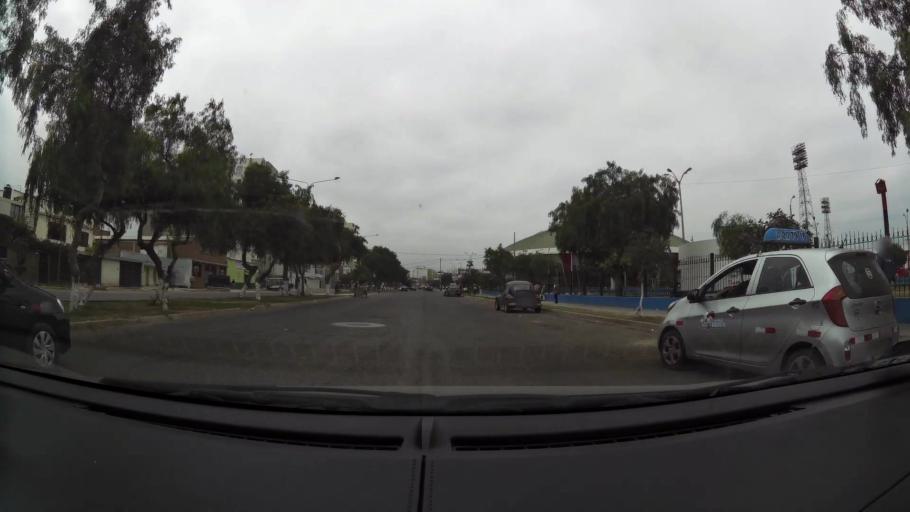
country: PE
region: La Libertad
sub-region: Provincia de Trujillo
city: Trujillo
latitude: -8.1057
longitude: -79.0327
